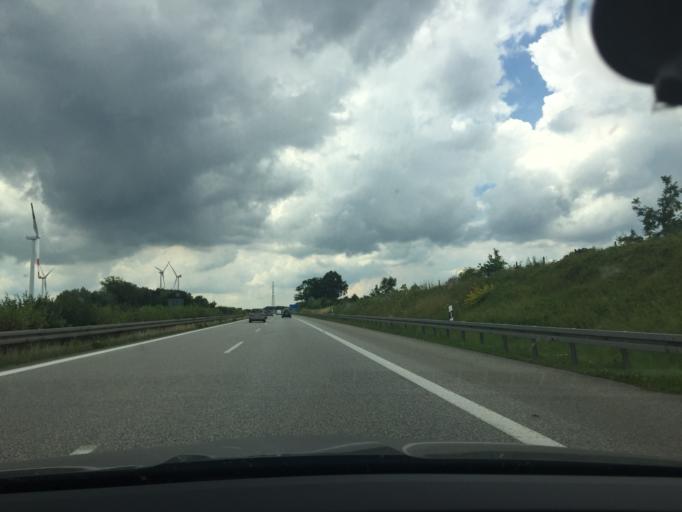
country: DE
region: Mecklenburg-Vorpommern
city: Jurgenshagen
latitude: 53.9630
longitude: 11.8780
